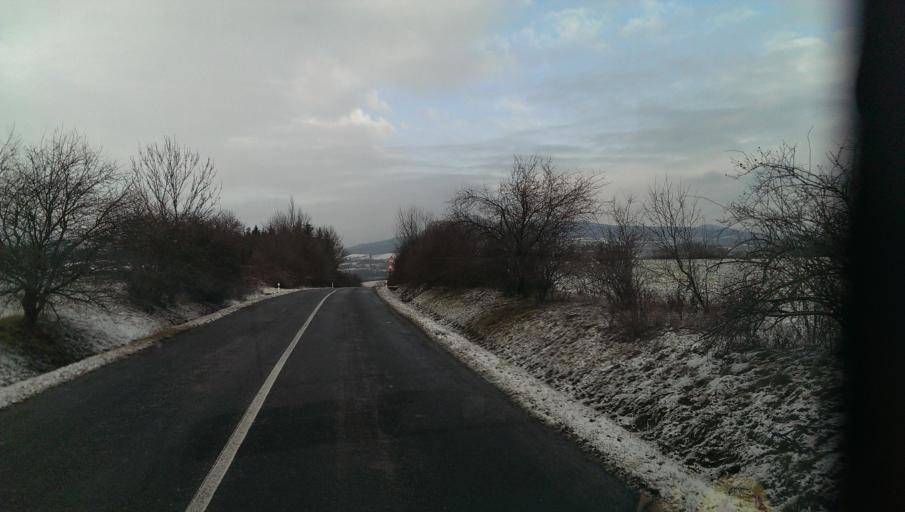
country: CZ
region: Ustecky
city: Trebenice
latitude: 50.4584
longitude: 13.9968
